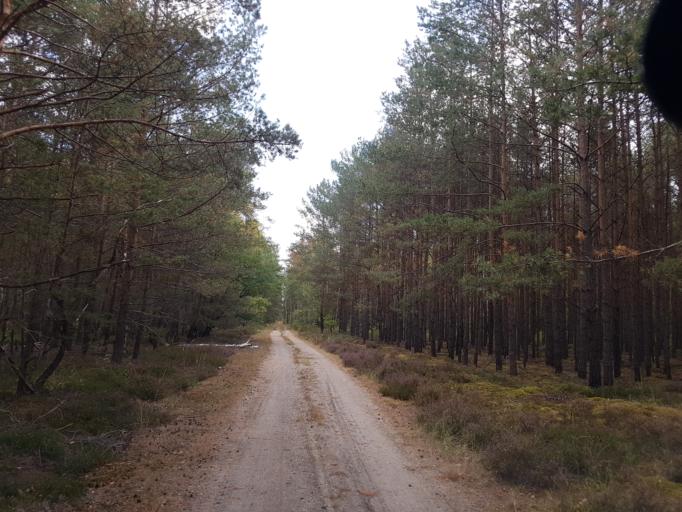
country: DE
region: Brandenburg
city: Finsterwalde
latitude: 51.5914
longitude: 13.7470
